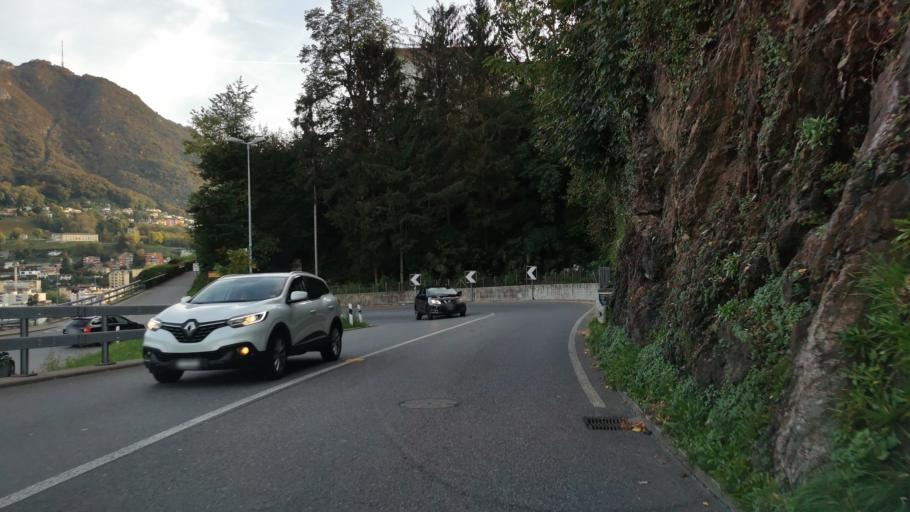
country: CH
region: Ticino
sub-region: Lugano District
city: Sorengo
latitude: 45.9953
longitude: 8.9419
